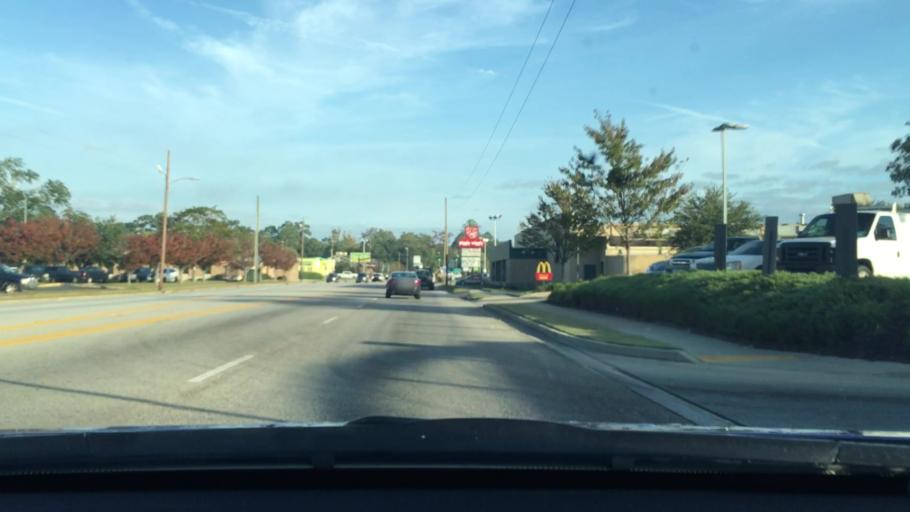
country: US
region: South Carolina
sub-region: Sumter County
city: Sumter
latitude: 33.9220
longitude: -80.3360
